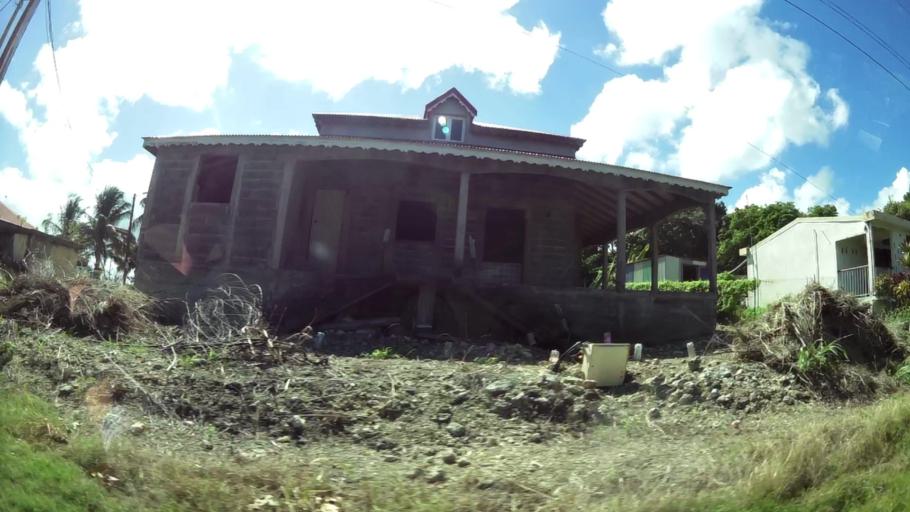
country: GP
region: Guadeloupe
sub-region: Guadeloupe
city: Le Moule
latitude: 16.3367
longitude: -61.3762
